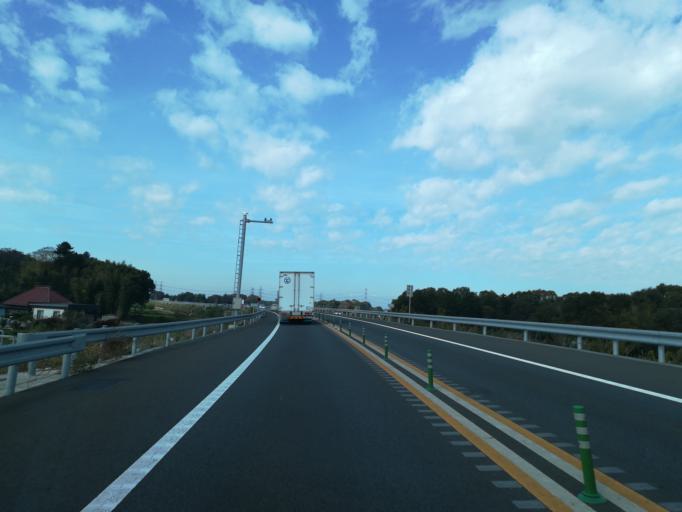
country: JP
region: Ibaraki
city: Sakai
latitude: 36.1096
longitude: 139.8588
